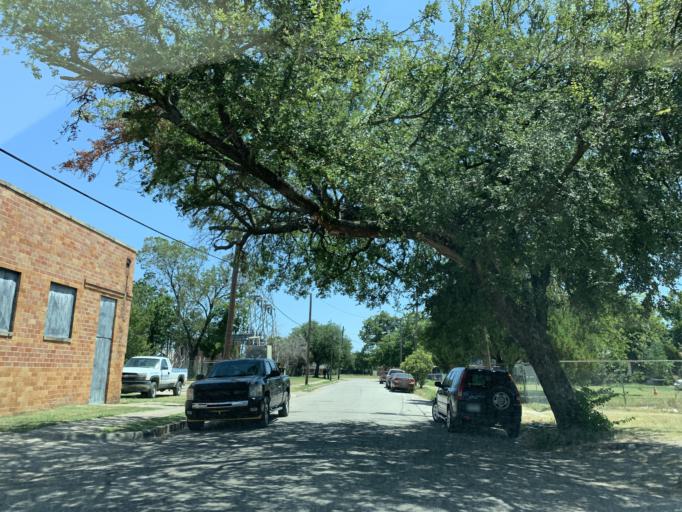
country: US
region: Texas
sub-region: Dallas County
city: Dallas
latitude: 32.7746
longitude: -96.7665
